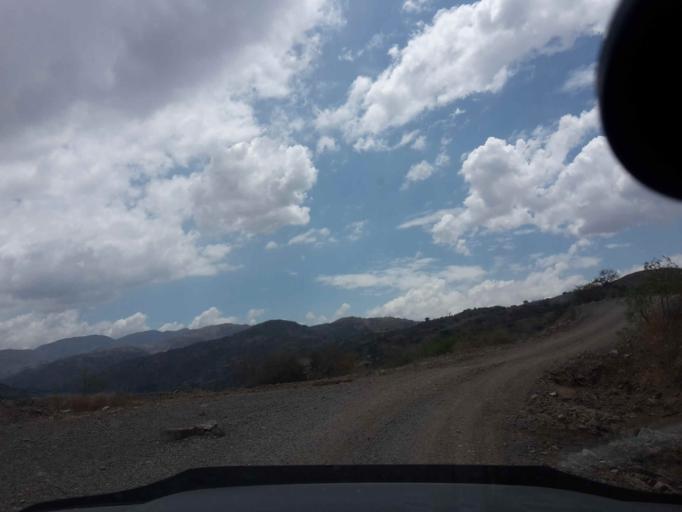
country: BO
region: Cochabamba
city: Sipe Sipe
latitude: -17.5485
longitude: -66.4801
